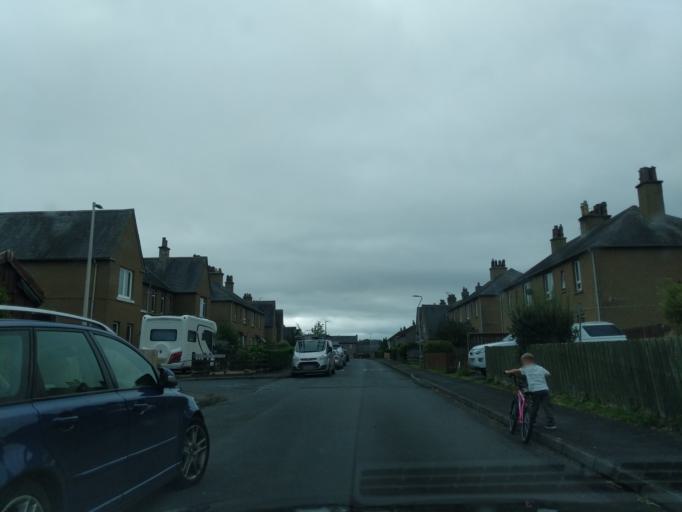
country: GB
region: Scotland
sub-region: The Scottish Borders
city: Saint Boswells
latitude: 55.5680
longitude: -2.6457
